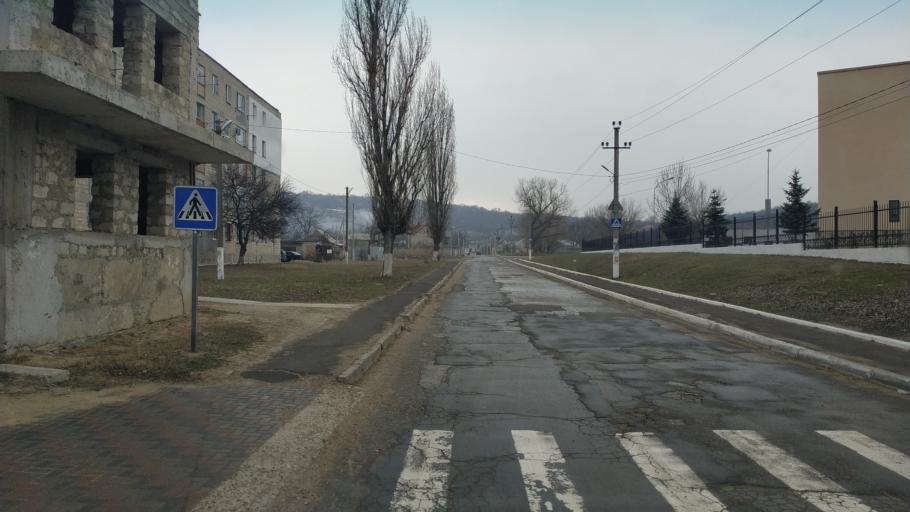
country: MD
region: Chisinau
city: Singera
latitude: 46.9150
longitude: 28.9746
